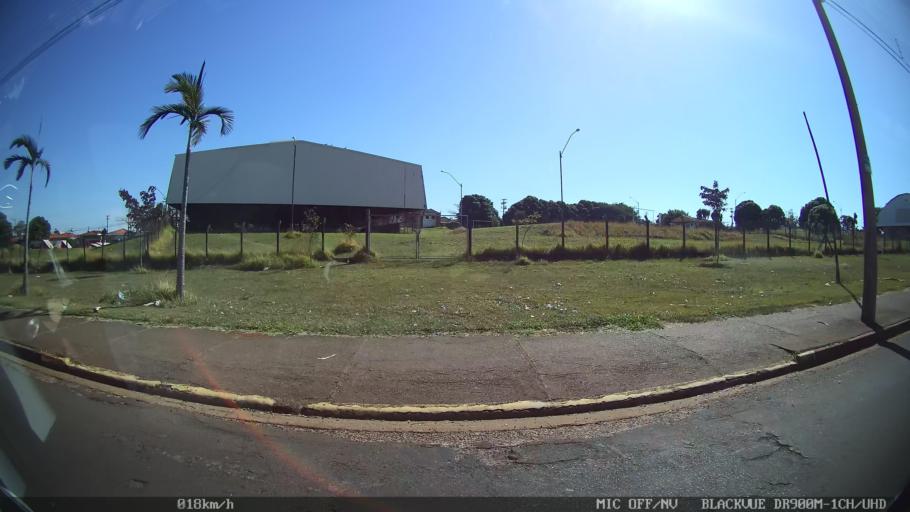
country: BR
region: Sao Paulo
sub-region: Batatais
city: Batatais
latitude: -20.8868
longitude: -47.5741
